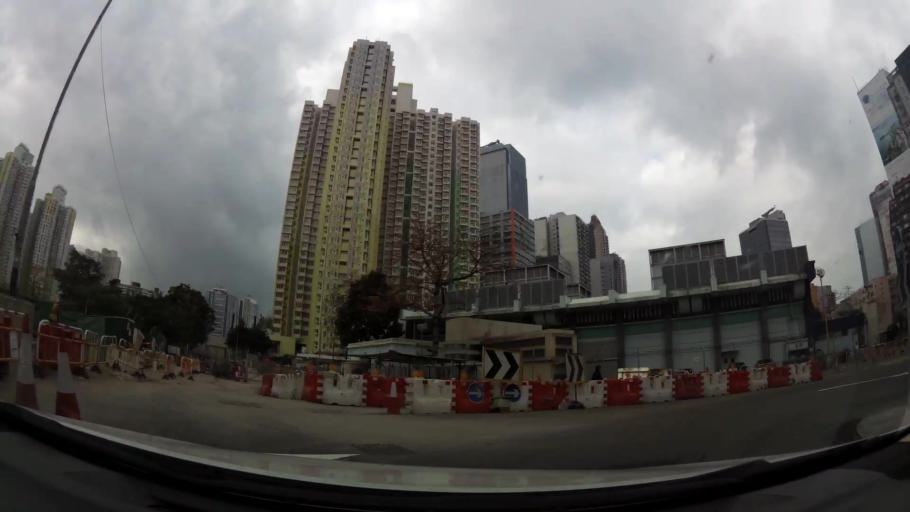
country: HK
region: Wong Tai Sin
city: Wong Tai Sin
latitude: 22.3363
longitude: 114.2009
